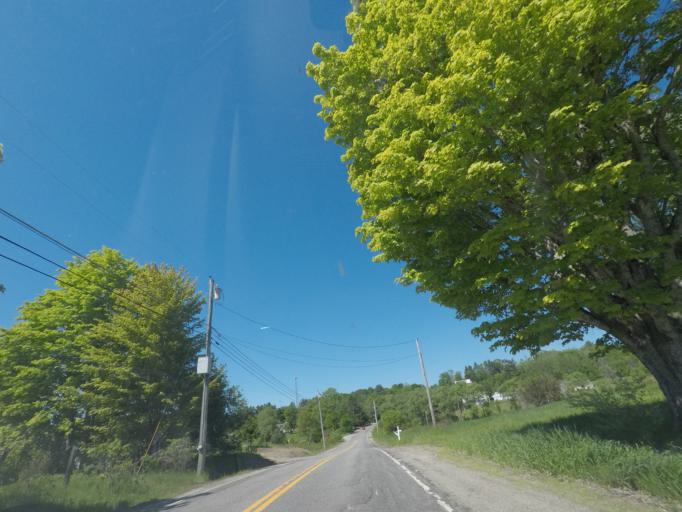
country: US
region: Maine
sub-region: Kennebec County
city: Gardiner
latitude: 44.2267
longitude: -69.8435
